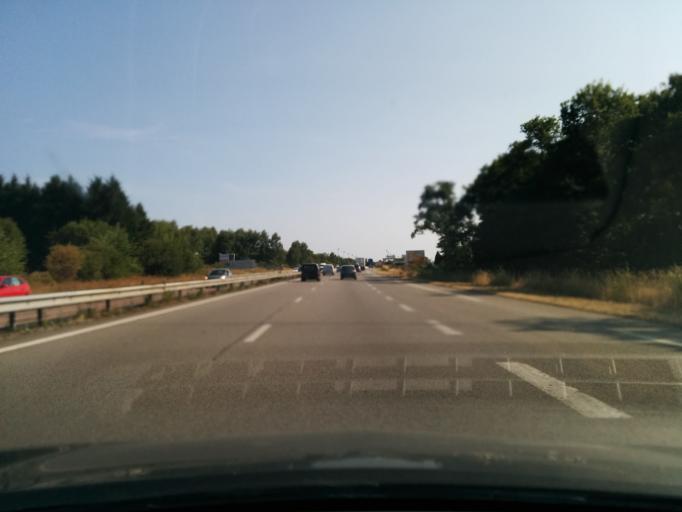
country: FR
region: Limousin
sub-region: Departement de la Haute-Vienne
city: Rilhac-Rancon
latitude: 45.8895
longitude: 1.2925
